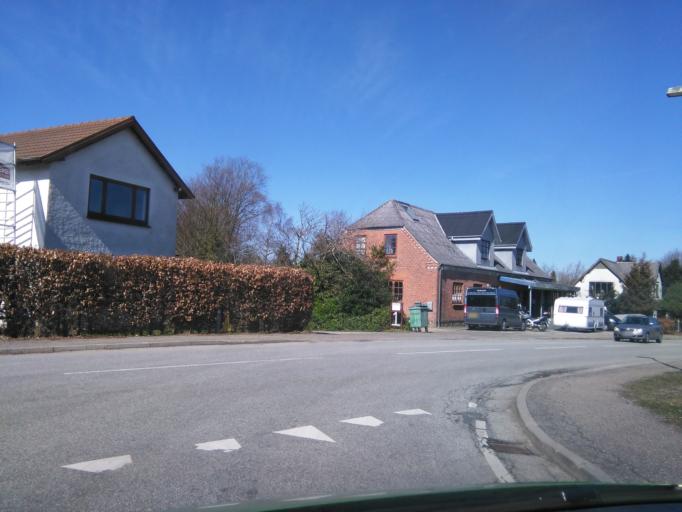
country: DK
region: Central Jutland
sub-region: Horsens Kommune
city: Braedstrup
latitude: 56.0209
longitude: 9.6423
